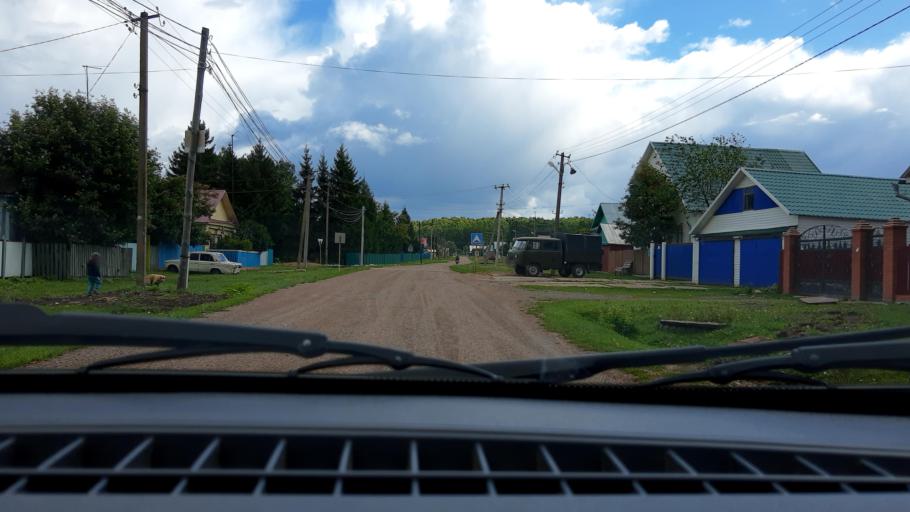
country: RU
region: Bashkortostan
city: Blagoveshchensk
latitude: 54.9471
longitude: 55.8701
